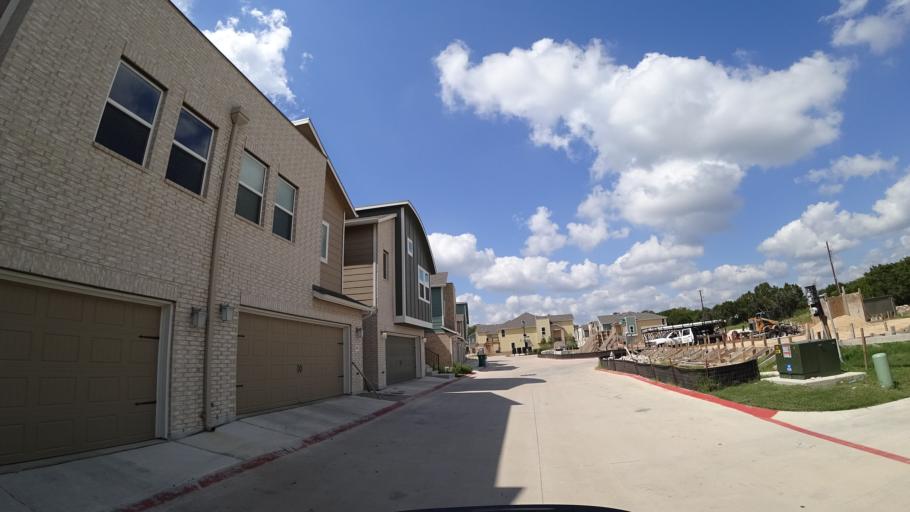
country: US
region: Texas
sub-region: Travis County
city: Onion Creek
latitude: 30.1842
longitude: -97.7829
